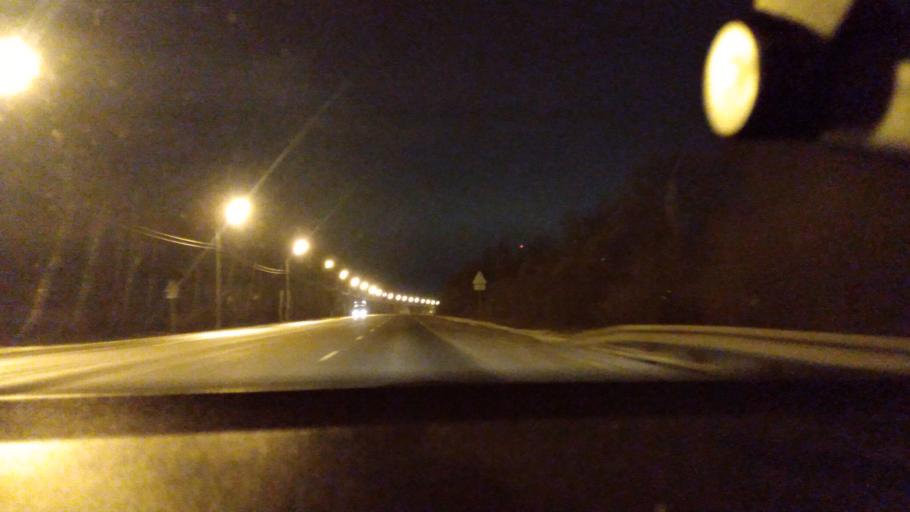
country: RU
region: Moskovskaya
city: Bronnitsy
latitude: 55.3895
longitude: 38.3356
